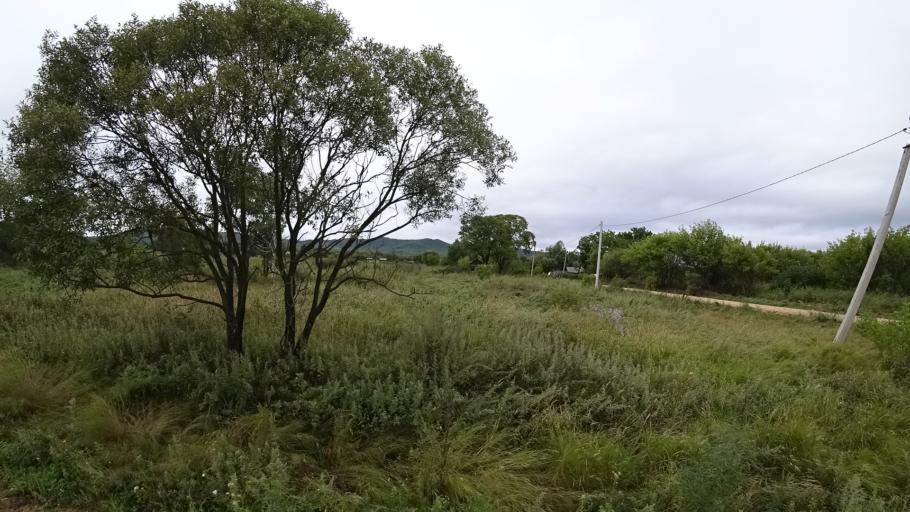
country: RU
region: Primorskiy
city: Rettikhovka
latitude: 44.1301
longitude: 132.6402
